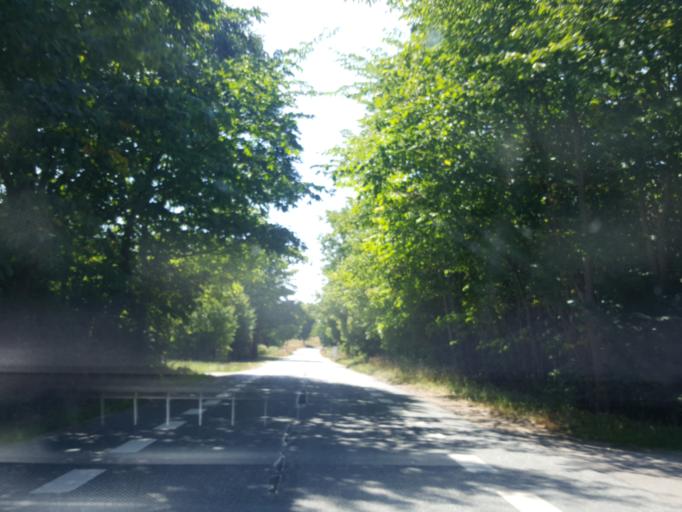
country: DK
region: Capital Region
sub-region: Allerod Kommune
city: Blovstrod
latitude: 55.9168
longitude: 12.4255
